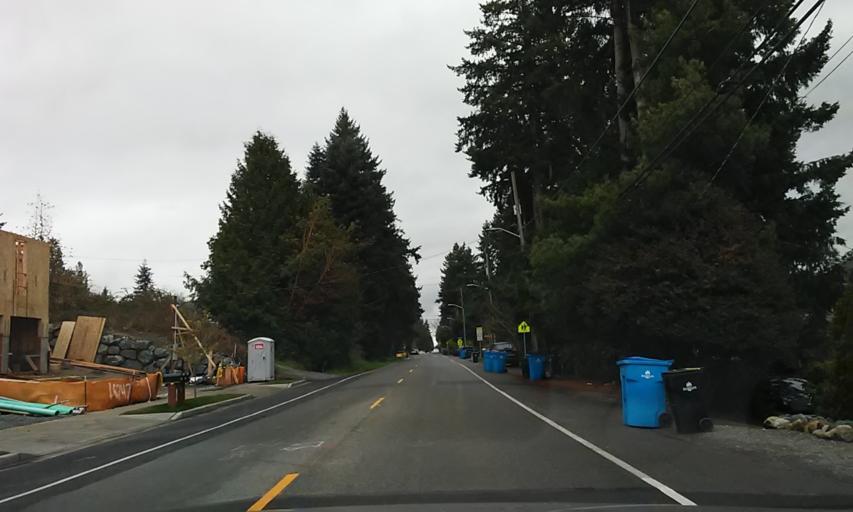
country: US
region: Washington
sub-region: King County
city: Shoreline
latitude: 47.7516
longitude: -122.3401
